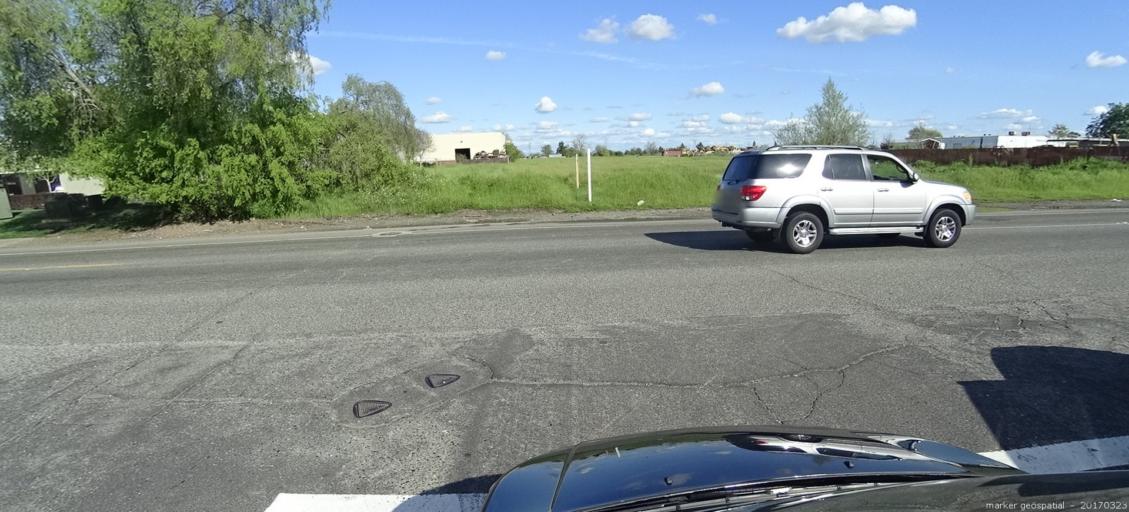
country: US
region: California
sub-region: Sacramento County
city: Rosemont
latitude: 38.5148
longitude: -121.3700
